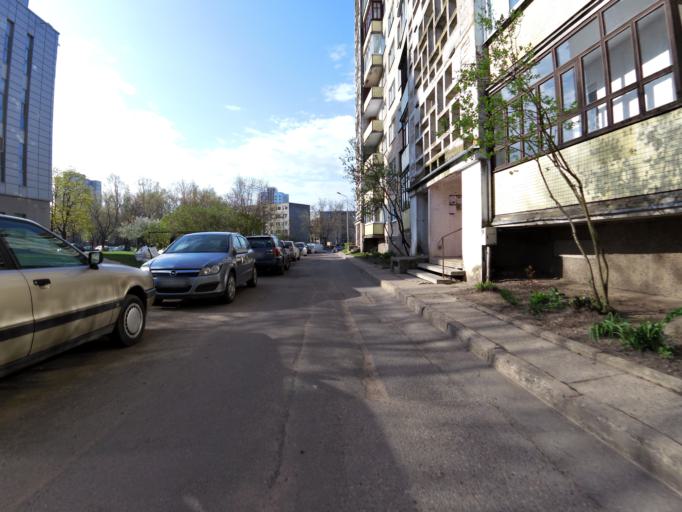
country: LT
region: Vilnius County
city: Lazdynai
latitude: 54.6838
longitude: 25.2110
